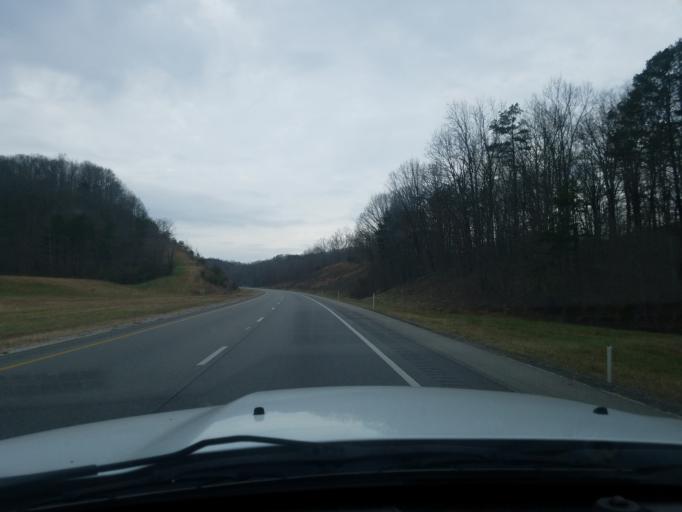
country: US
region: Kentucky
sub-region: Carter County
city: Grayson
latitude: 38.3653
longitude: -82.8771
